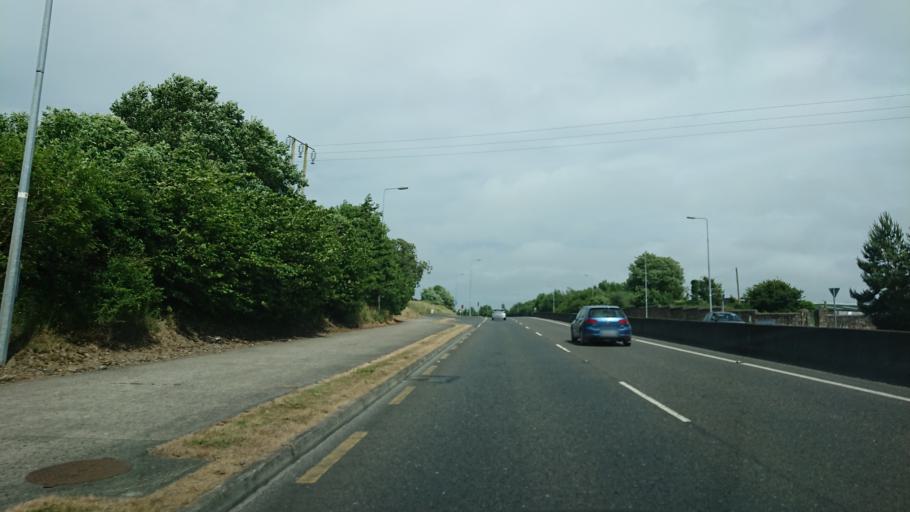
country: IE
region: Munster
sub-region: Waterford
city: Waterford
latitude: 52.2368
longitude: -7.0971
